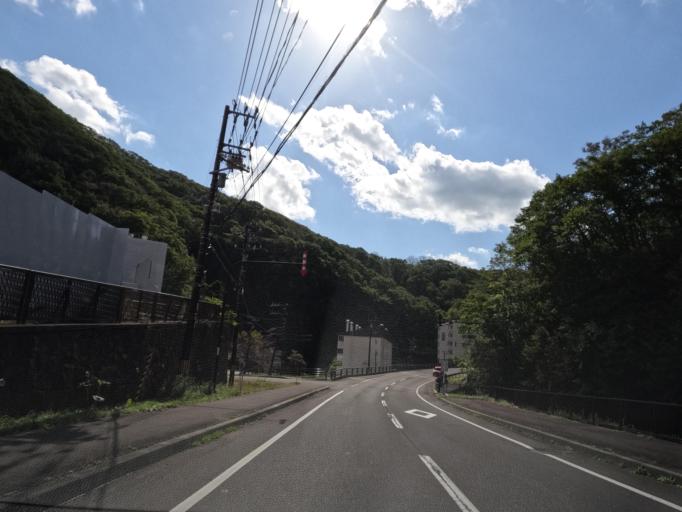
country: JP
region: Hokkaido
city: Shiraoi
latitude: 42.4880
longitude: 141.1477
